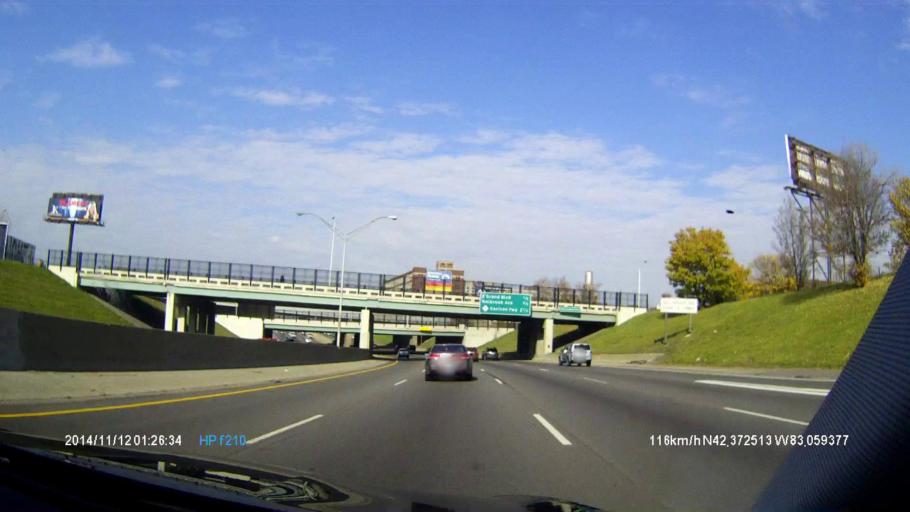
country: US
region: Michigan
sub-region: Wayne County
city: Hamtramck
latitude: 42.3731
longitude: -83.0595
